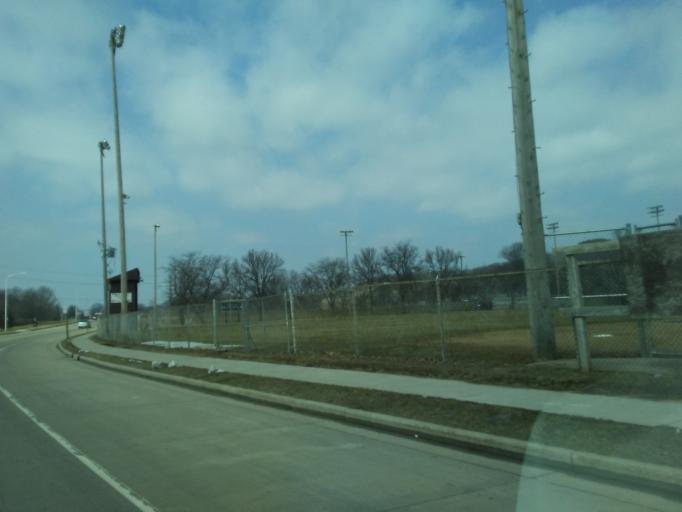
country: US
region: Wisconsin
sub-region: Richland County
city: Richland Center
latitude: 43.3429
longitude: -90.3899
